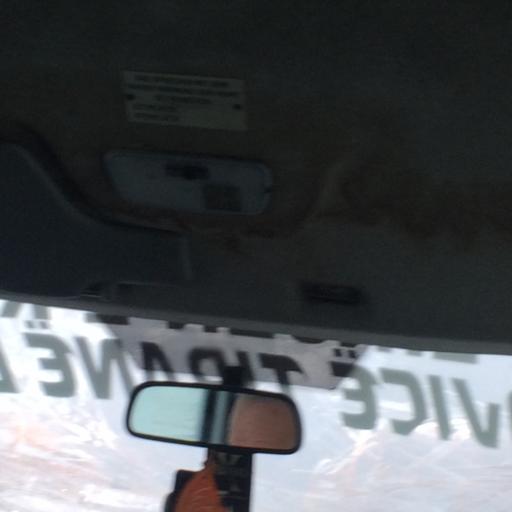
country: XK
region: Pristina
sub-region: Komuna e Drenasit
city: Glogovac
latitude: 42.5865
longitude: 20.8952
